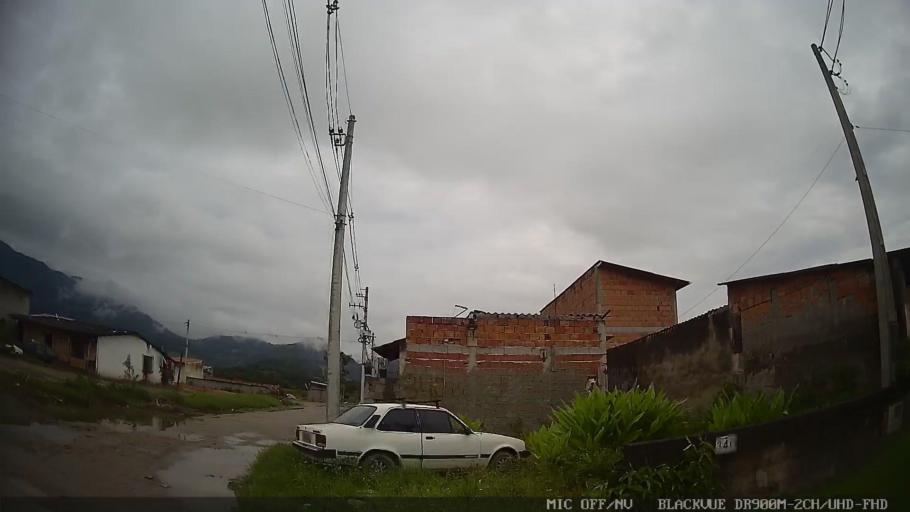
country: BR
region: Sao Paulo
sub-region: Sao Sebastiao
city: Sao Sebastiao
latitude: -23.7109
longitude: -45.4555
